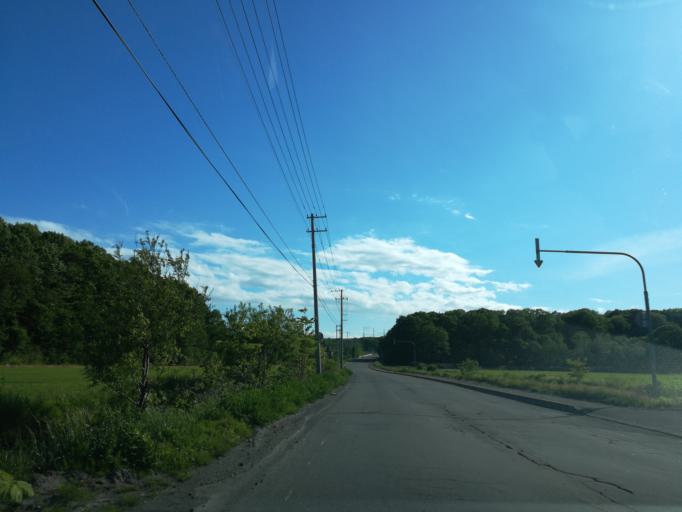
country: JP
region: Hokkaido
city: Kitahiroshima
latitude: 43.0034
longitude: 141.5491
